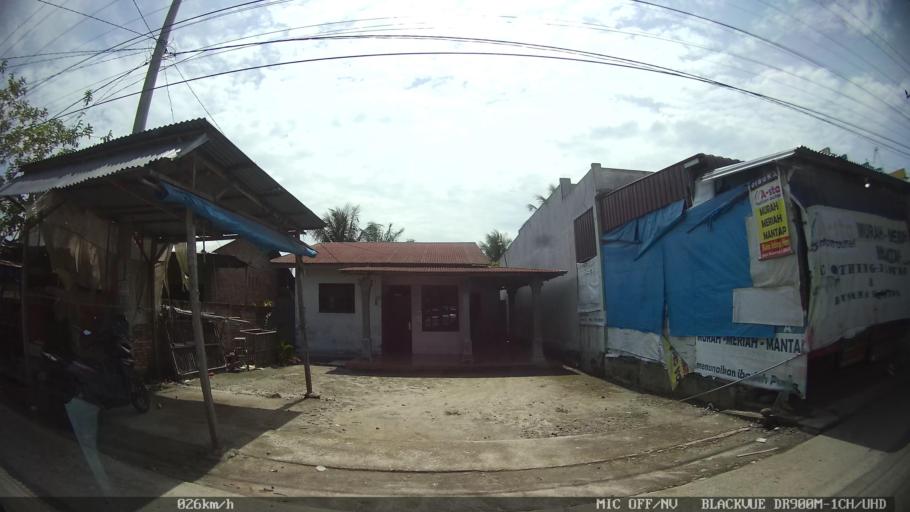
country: ID
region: North Sumatra
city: Percut
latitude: 3.5998
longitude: 98.8604
